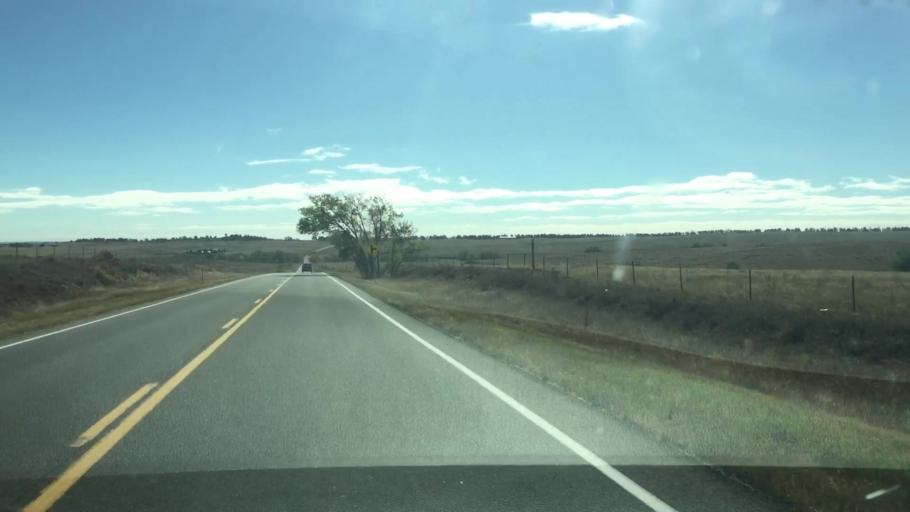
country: US
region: Colorado
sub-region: Elbert County
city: Kiowa
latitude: 39.3262
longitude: -104.3968
